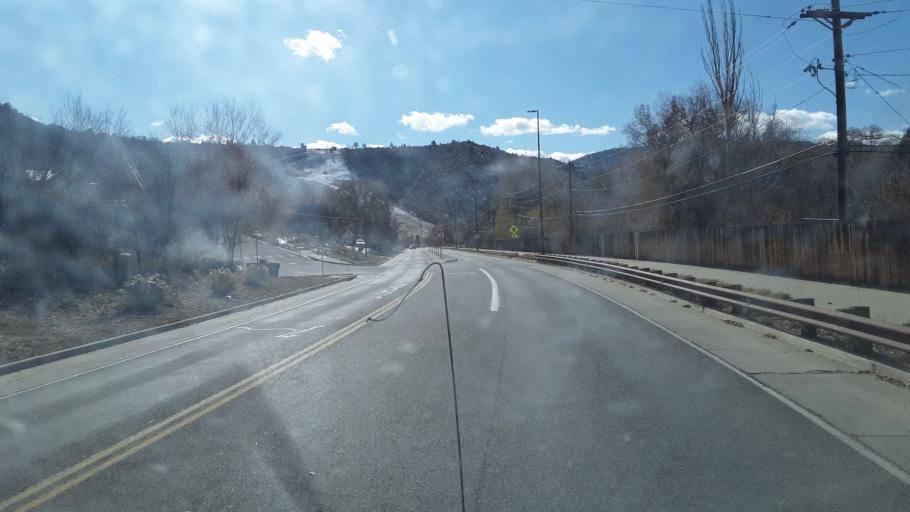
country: US
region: Colorado
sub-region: La Plata County
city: Durango
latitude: 37.2872
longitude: -107.8662
